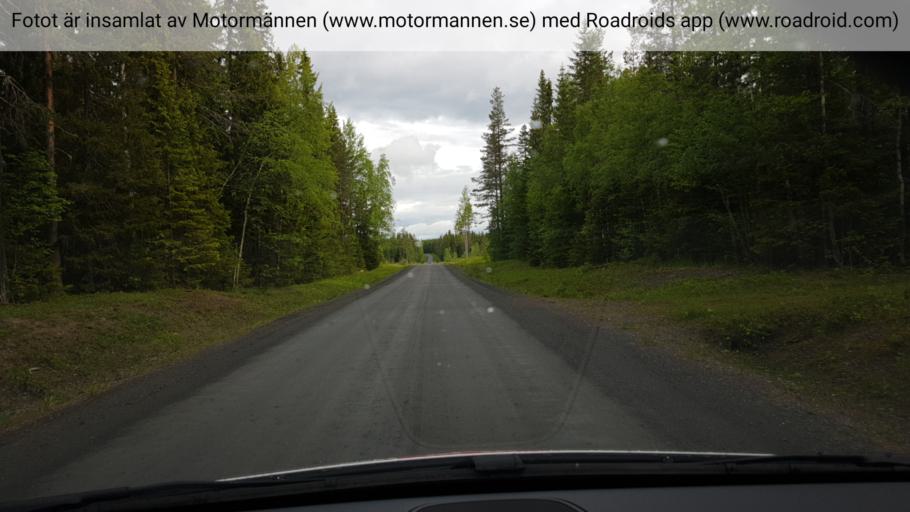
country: SE
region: Jaemtland
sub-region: OEstersunds Kommun
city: Brunflo
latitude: 63.2115
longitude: 15.0949
